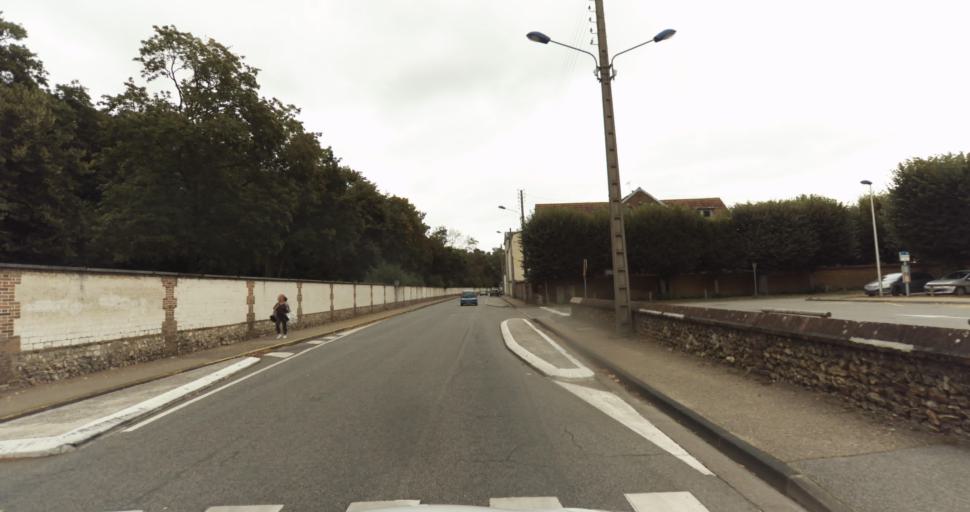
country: FR
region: Haute-Normandie
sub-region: Departement de l'Eure
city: Evreux
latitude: 49.0183
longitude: 1.1258
